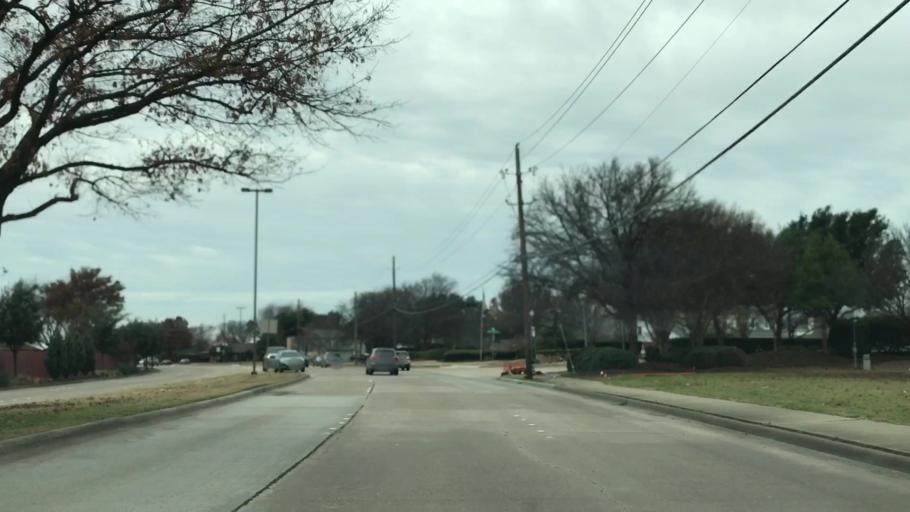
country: US
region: Texas
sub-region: Dallas County
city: Carrollton
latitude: 33.0173
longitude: -96.8863
